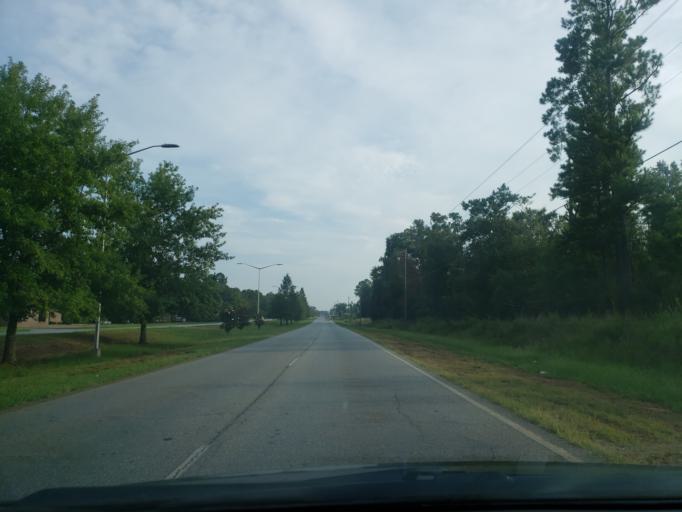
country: US
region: Georgia
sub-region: Dougherty County
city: Albany
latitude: 31.5793
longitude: -84.2193
